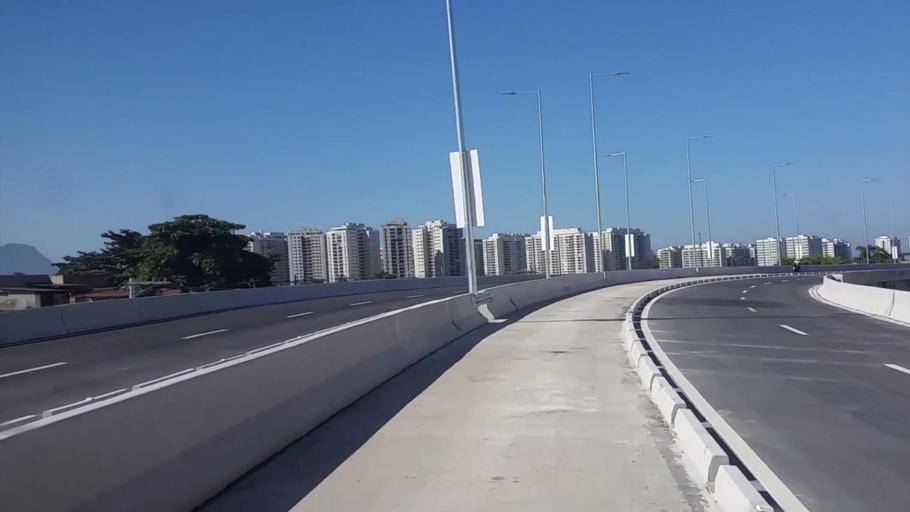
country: BR
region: Rio de Janeiro
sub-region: Nilopolis
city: Nilopolis
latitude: -22.9591
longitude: -43.3923
